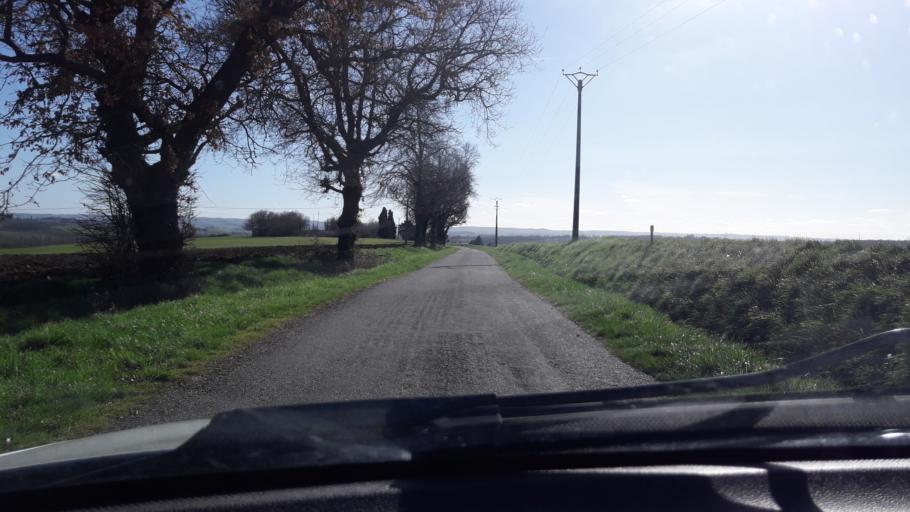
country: FR
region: Midi-Pyrenees
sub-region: Departement du Gers
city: Gimont
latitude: 43.6478
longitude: 1.0171
